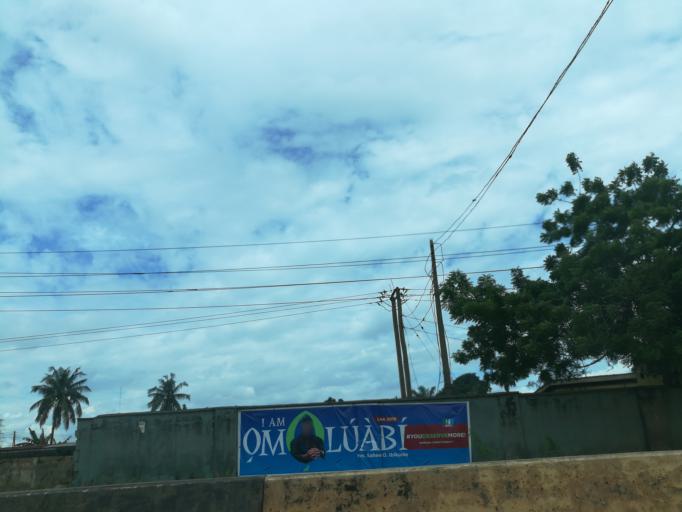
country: NG
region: Lagos
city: Ikorodu
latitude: 6.6281
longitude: 3.5068
